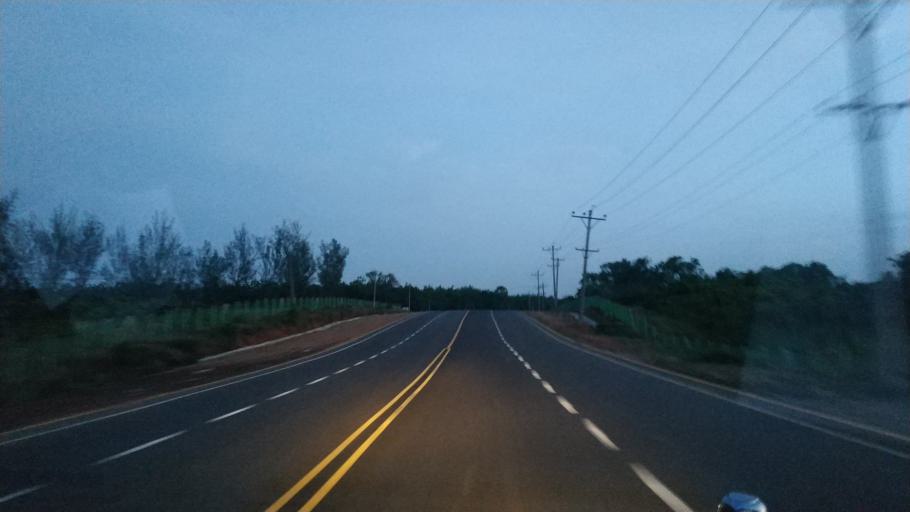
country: MM
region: Mon
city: Kyaikto
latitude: 17.3780
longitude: 97.0531
